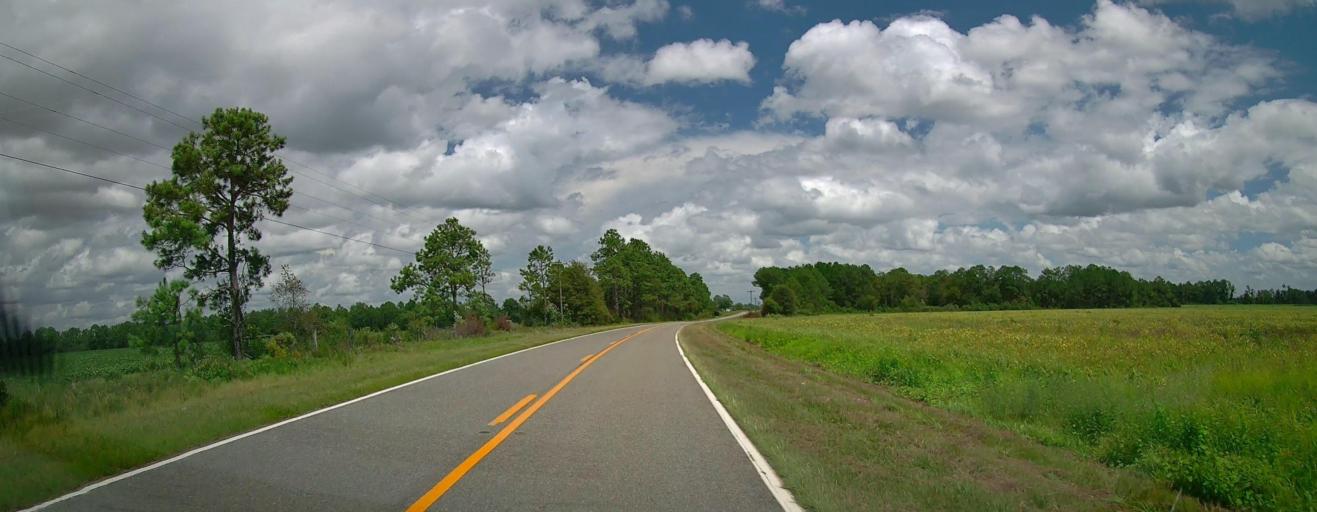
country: US
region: Georgia
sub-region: Irwin County
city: Ocilla
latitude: 31.6468
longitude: -83.3014
